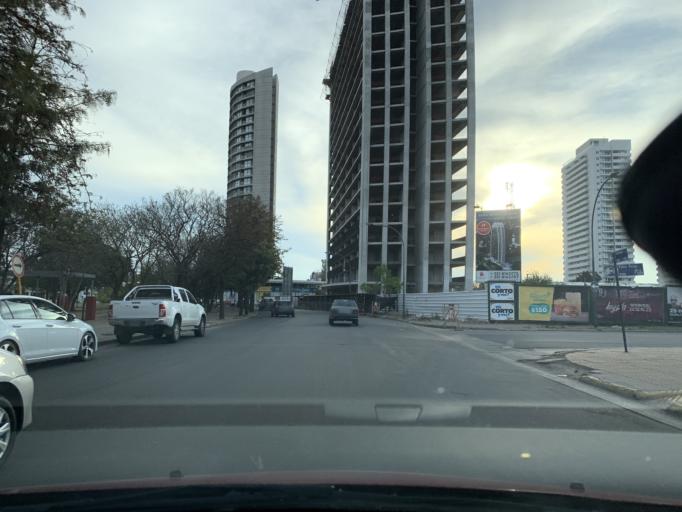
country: AR
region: Cordoba
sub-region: Departamento de Capital
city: Cordoba
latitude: -31.4093
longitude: -64.1713
